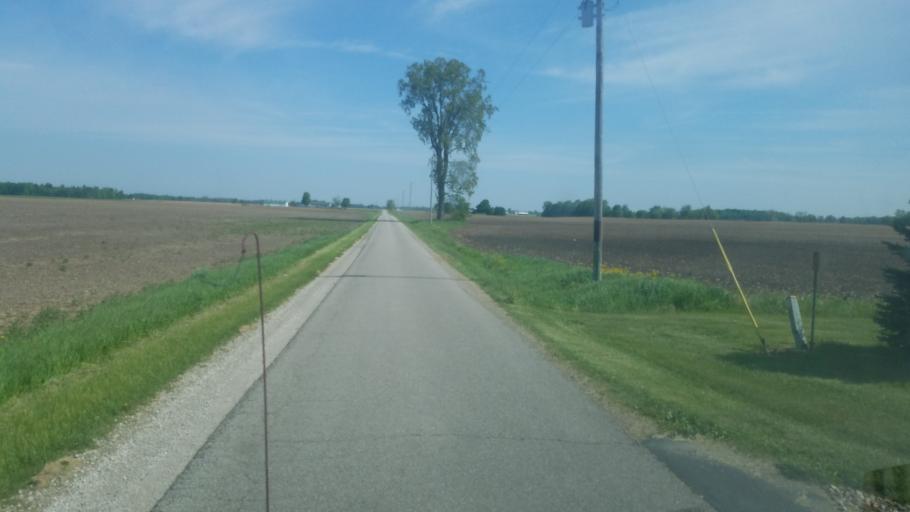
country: US
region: Ohio
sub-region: Crawford County
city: Bucyrus
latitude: 40.7833
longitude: -83.0737
